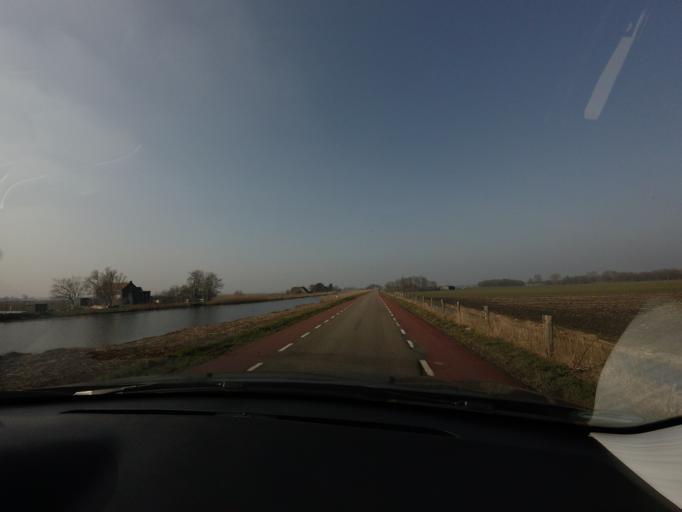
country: NL
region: North Holland
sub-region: Gemeente Opmeer
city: Opmeer
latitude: 52.6176
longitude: 4.9323
